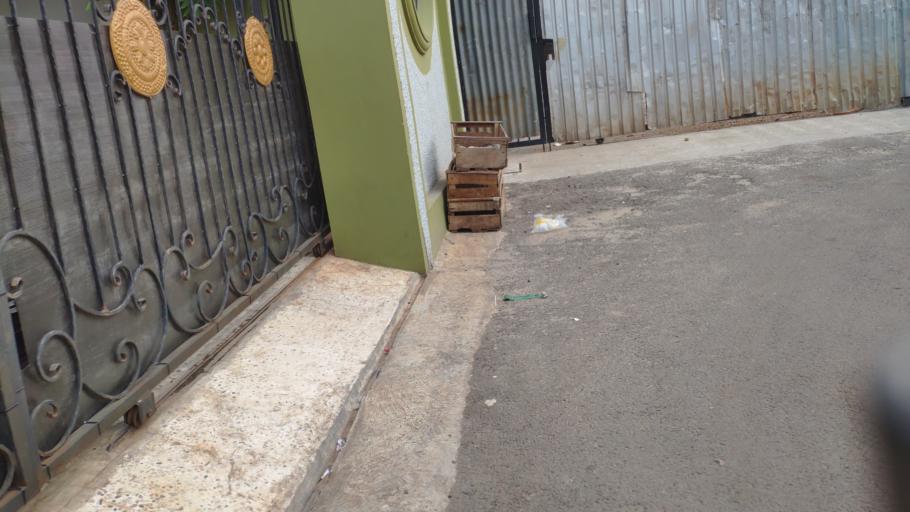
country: ID
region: West Java
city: Pamulang
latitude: -6.3134
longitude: 106.8070
